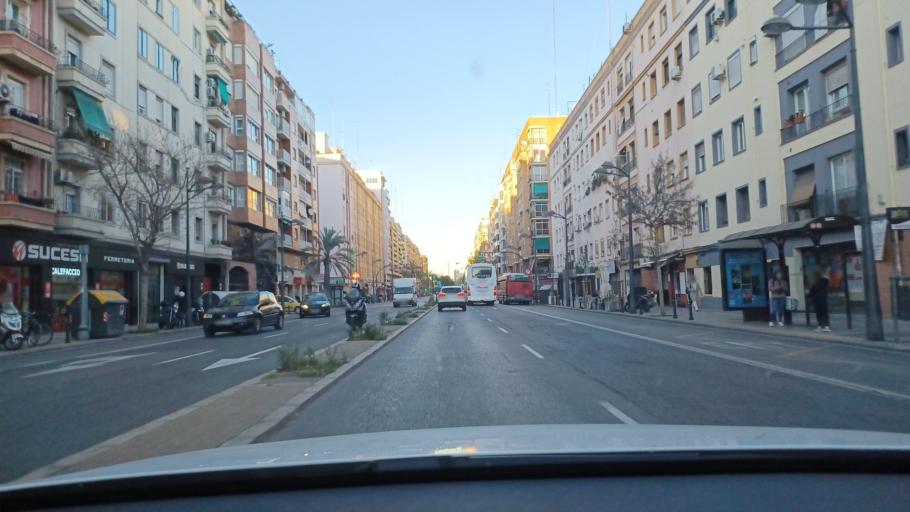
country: ES
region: Valencia
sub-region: Provincia de Valencia
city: Valencia
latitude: 39.4719
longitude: -0.3541
